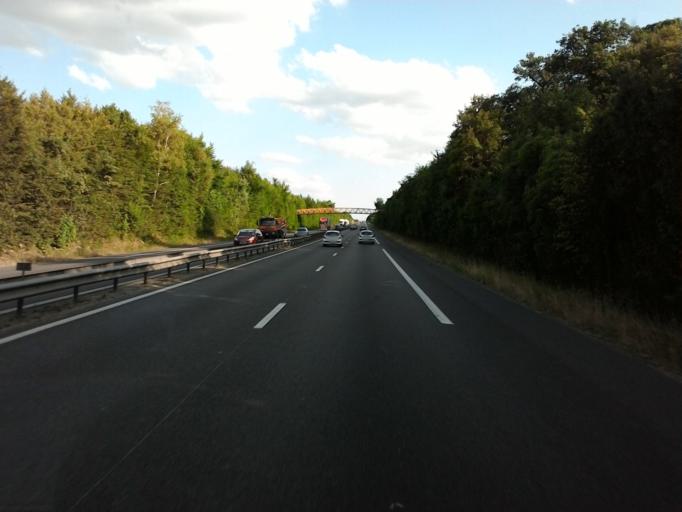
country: FR
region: Lorraine
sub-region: Departement de Meurthe-et-Moselle
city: Laxou
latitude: 48.6756
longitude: 6.1205
